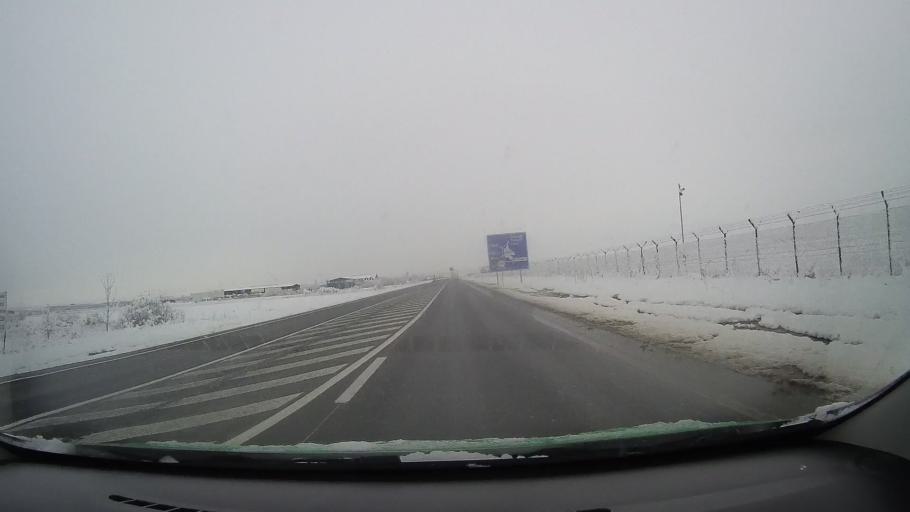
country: RO
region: Sibiu
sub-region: Comuna Cristian
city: Cristian
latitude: 45.7888
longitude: 24.0661
